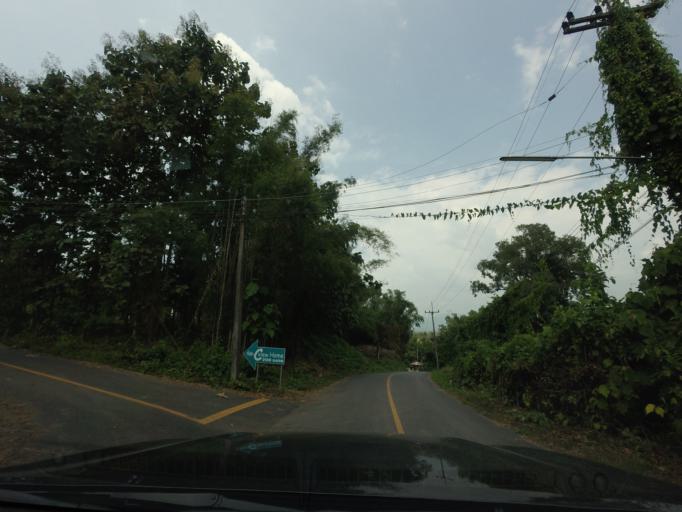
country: TH
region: Nan
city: Pua
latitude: 19.1691
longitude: 100.9272
